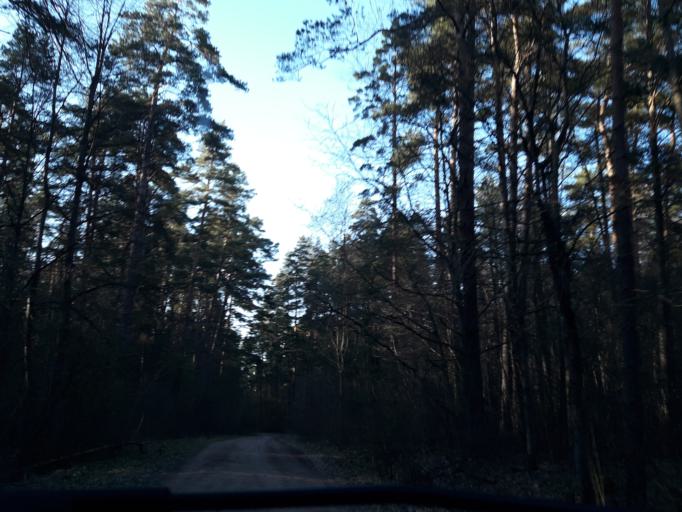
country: LV
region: Kekava
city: Kekava
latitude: 56.8561
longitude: 24.2320
